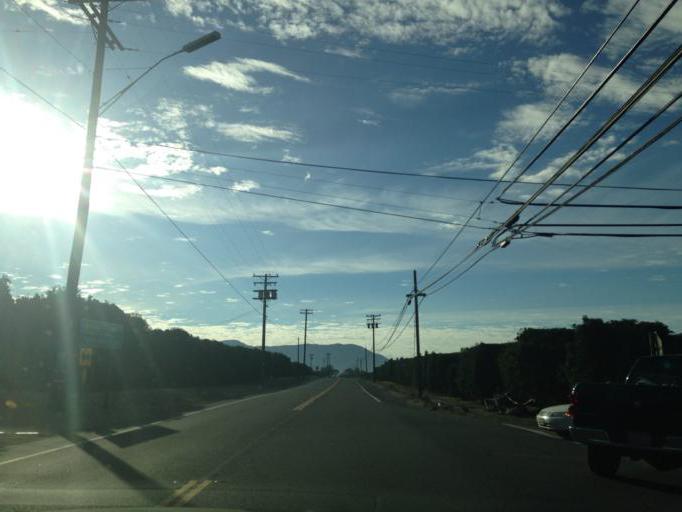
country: US
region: California
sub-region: San Diego County
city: Valley Center
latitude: 33.3191
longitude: -116.9931
